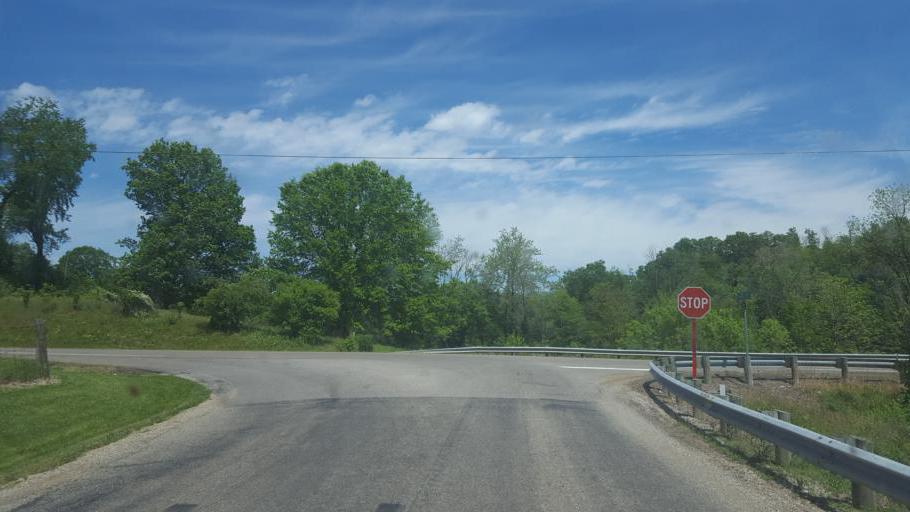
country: US
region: Ohio
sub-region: Knox County
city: Danville
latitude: 40.4063
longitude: -82.3219
